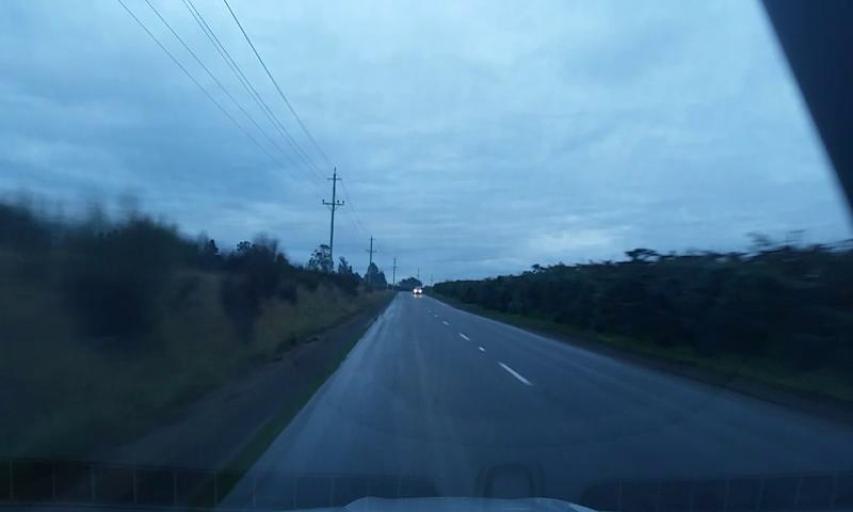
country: NZ
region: Canterbury
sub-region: Ashburton District
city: Rakaia
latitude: -43.7584
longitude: 171.9568
